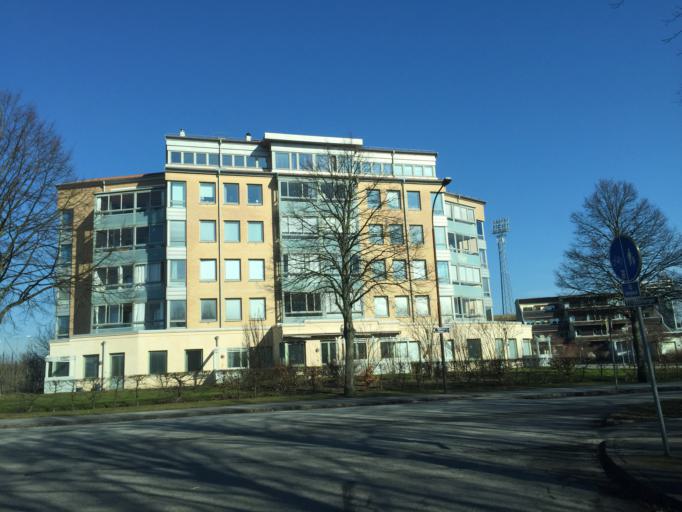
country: SE
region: Skane
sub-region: Lunds Kommun
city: Lund
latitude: 55.6947
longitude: 13.1759
